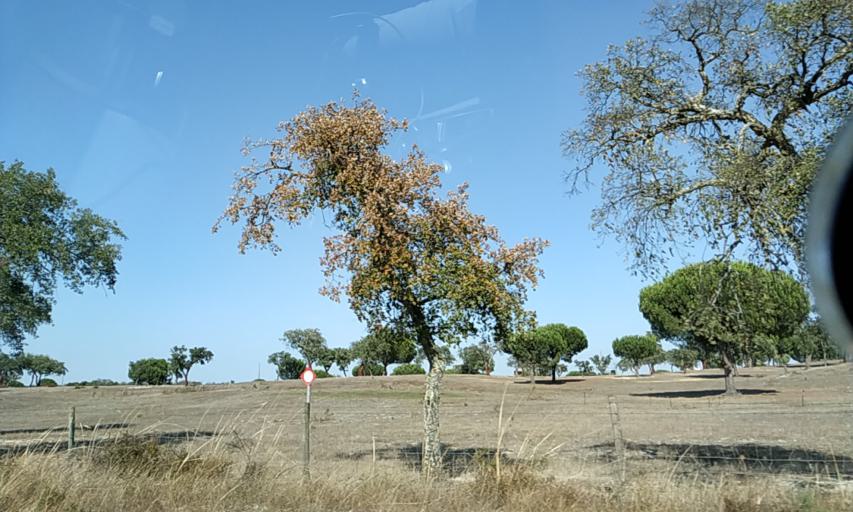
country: PT
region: Santarem
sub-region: Coruche
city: Coruche
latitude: 38.8563
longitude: -8.5451
